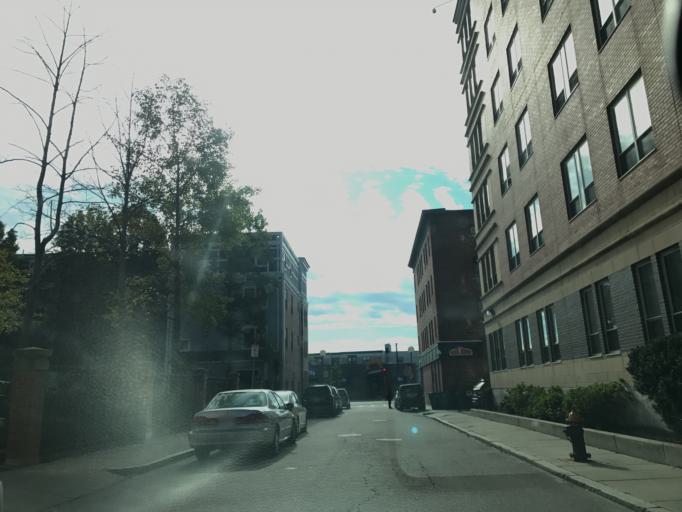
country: US
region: Massachusetts
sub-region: Suffolk County
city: Boston
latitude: 42.3379
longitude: -71.0843
